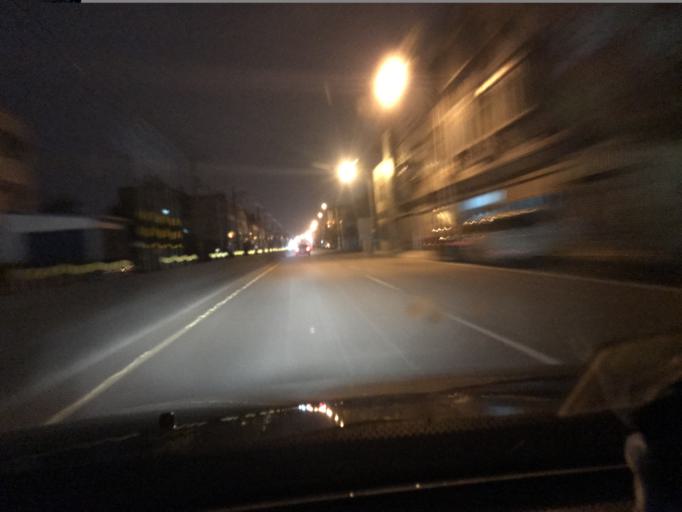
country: TW
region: Taiwan
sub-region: Hsinchu
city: Zhubei
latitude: 24.7876
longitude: 121.0647
